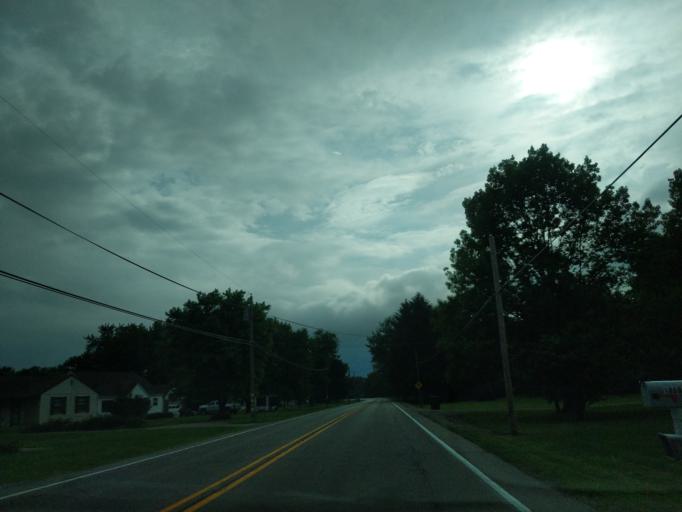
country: US
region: Indiana
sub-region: Delaware County
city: Yorktown
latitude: 40.1672
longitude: -85.5128
